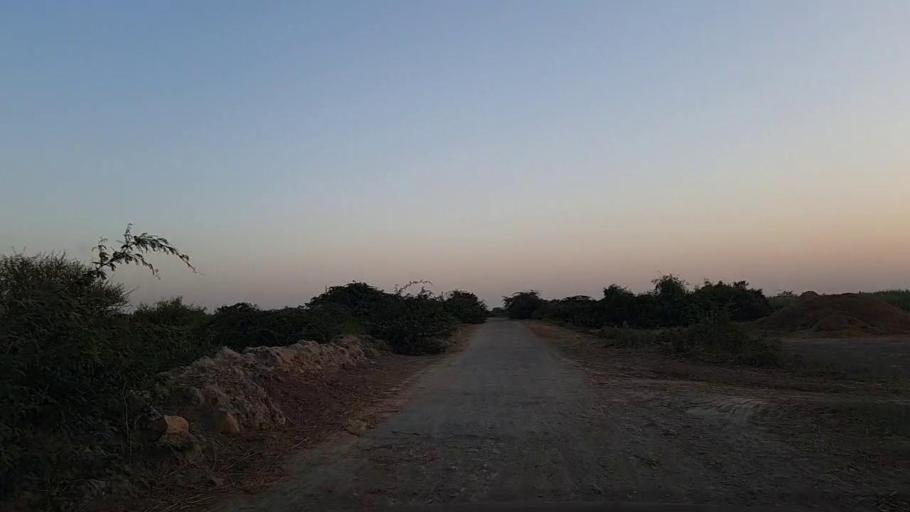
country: PK
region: Sindh
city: Mirpur Batoro
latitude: 24.6278
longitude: 68.1840
